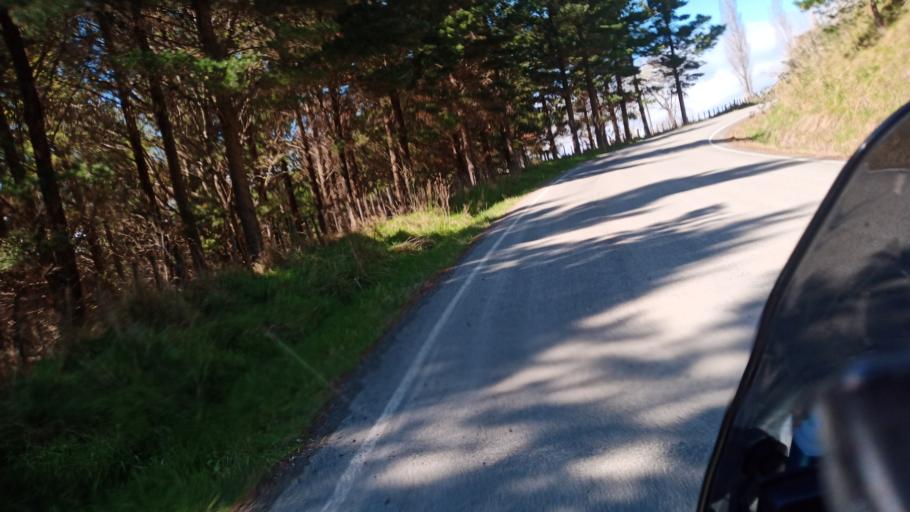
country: NZ
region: Gisborne
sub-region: Gisborne District
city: Gisborne
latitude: -38.8001
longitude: 177.7710
